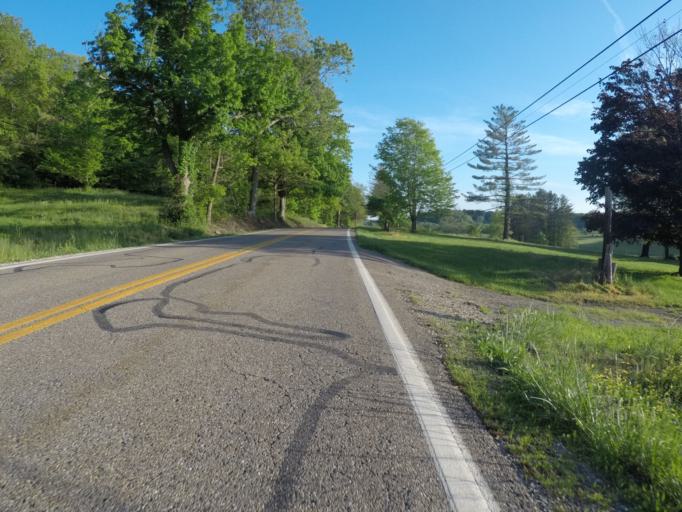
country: US
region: West Virginia
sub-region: Cabell County
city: Huntington
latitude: 38.5483
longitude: -82.4629
